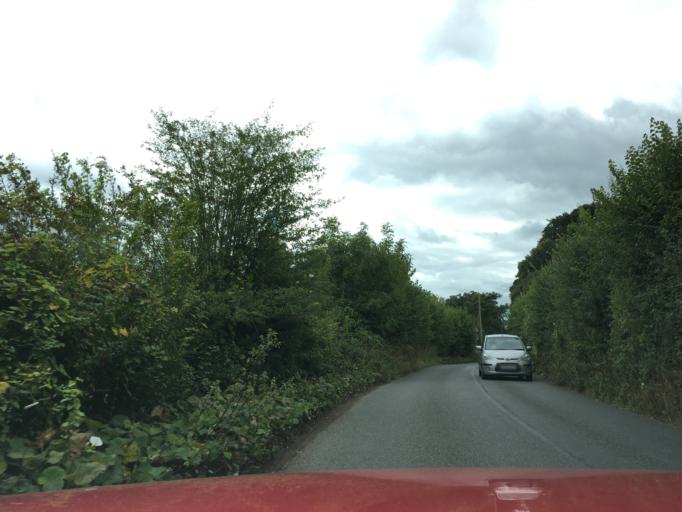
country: GB
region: England
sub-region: Devon
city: Starcross
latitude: 50.6077
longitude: -3.4455
